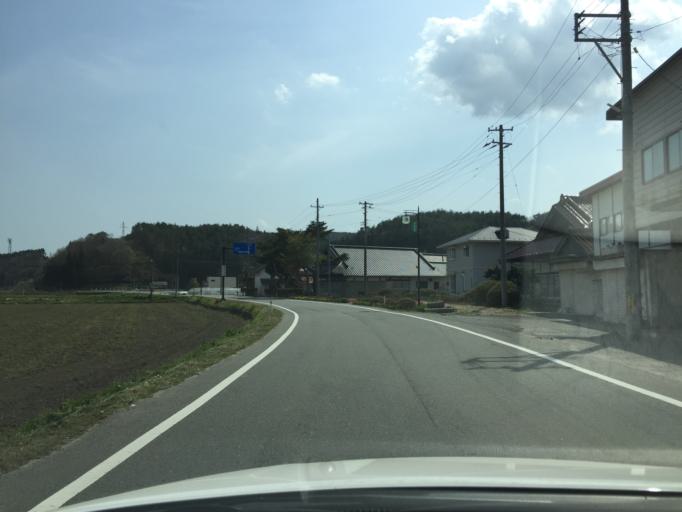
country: JP
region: Fukushima
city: Namie
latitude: 37.3144
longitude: 140.8342
